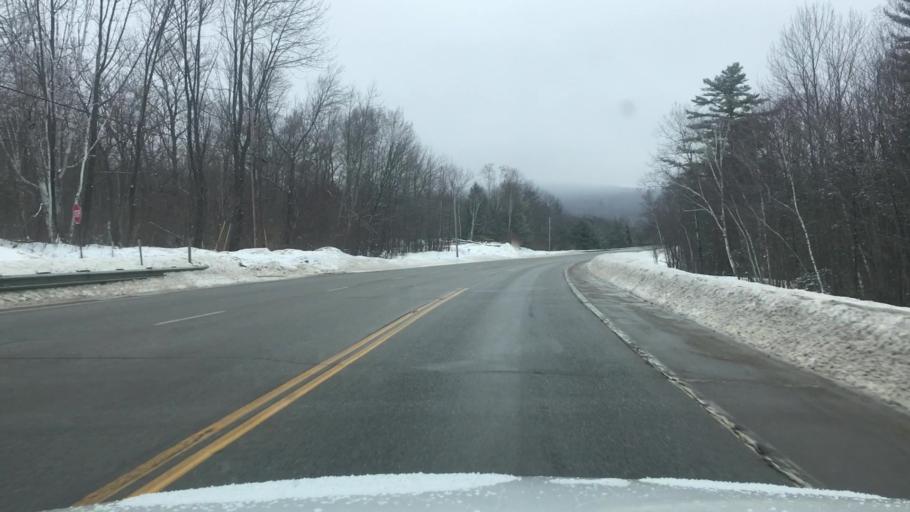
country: US
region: Maine
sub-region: Oxford County
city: Peru
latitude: 44.5873
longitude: -70.3653
